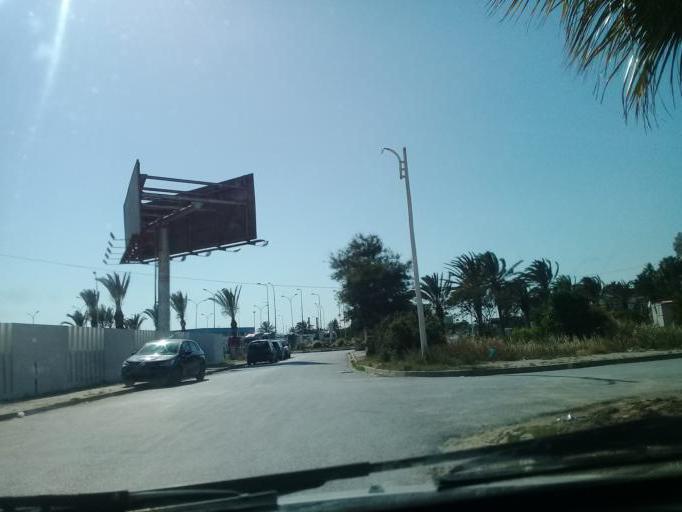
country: TN
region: Tunis
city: La Goulette
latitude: 36.8125
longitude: 10.3053
